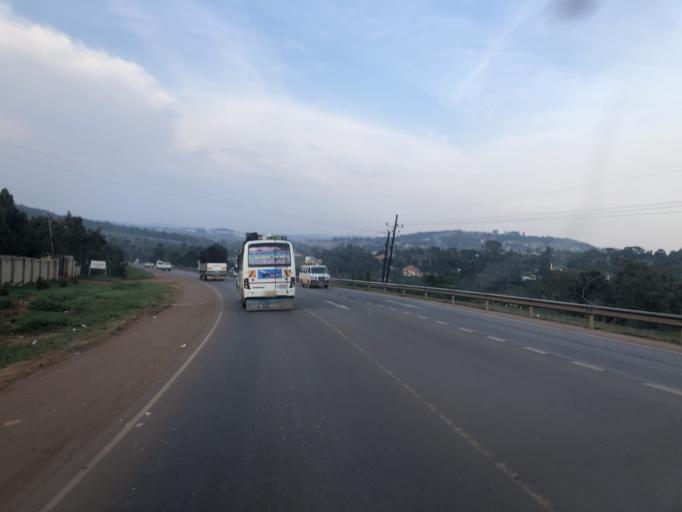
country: UG
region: Central Region
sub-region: Mpigi District
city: Mpigi
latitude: 0.2444
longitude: 32.3812
